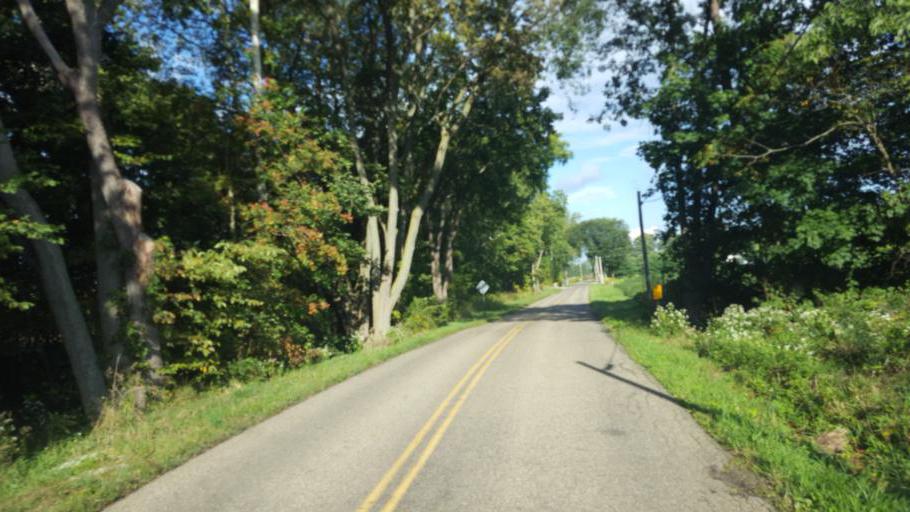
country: US
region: Ohio
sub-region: Knox County
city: Fredericktown
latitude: 40.4247
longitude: -82.5646
